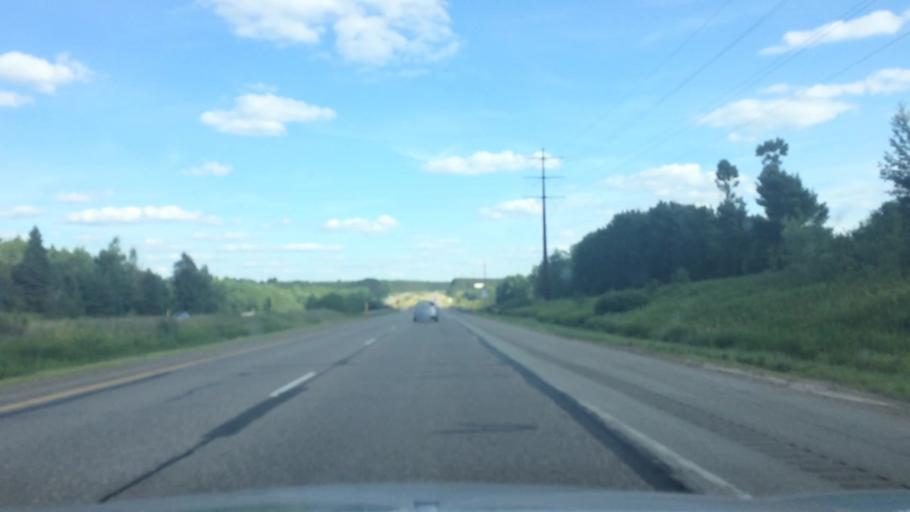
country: US
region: Wisconsin
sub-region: Lincoln County
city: Merrill
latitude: 45.2065
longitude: -89.6625
